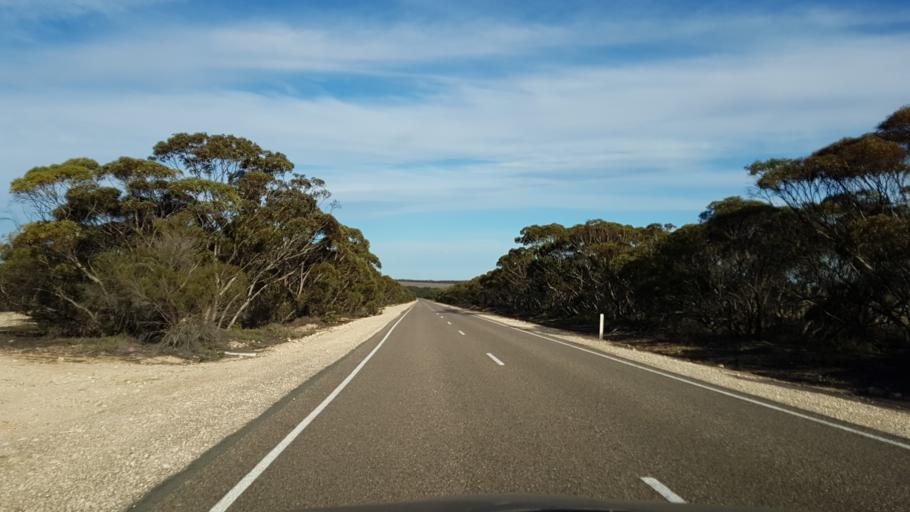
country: AU
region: South Australia
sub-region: Mid Murray
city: Mannum
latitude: -35.0304
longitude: 139.4895
